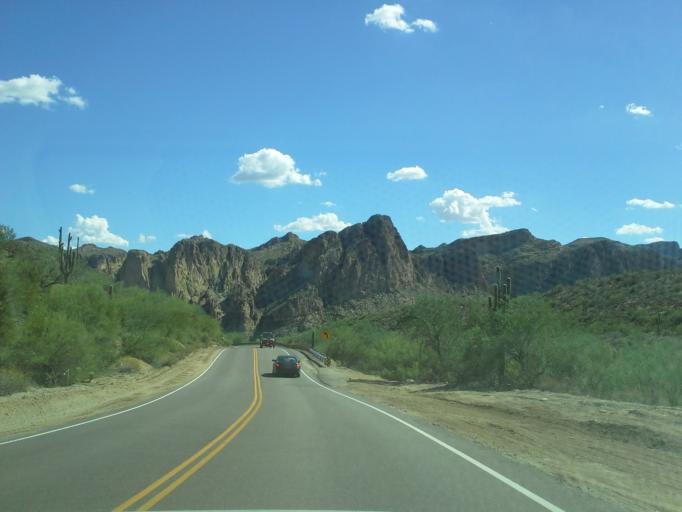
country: US
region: Arizona
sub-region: Pinal County
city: Apache Junction
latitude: 33.5643
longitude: -111.5433
